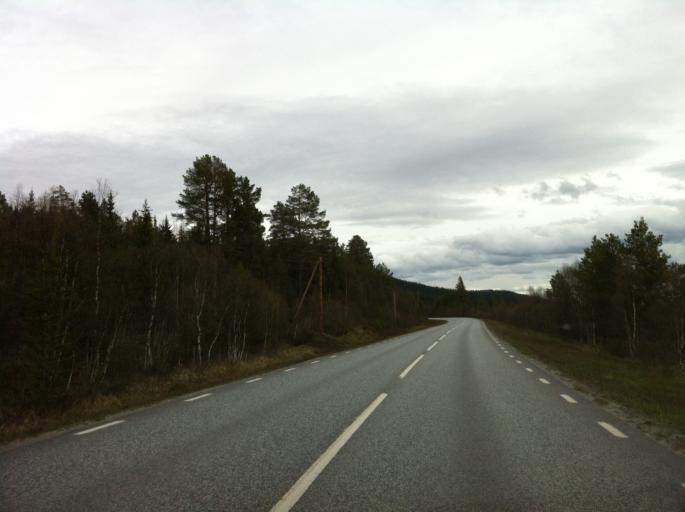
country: NO
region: Sor-Trondelag
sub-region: Tydal
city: Aas
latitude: 62.6138
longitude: 12.4961
